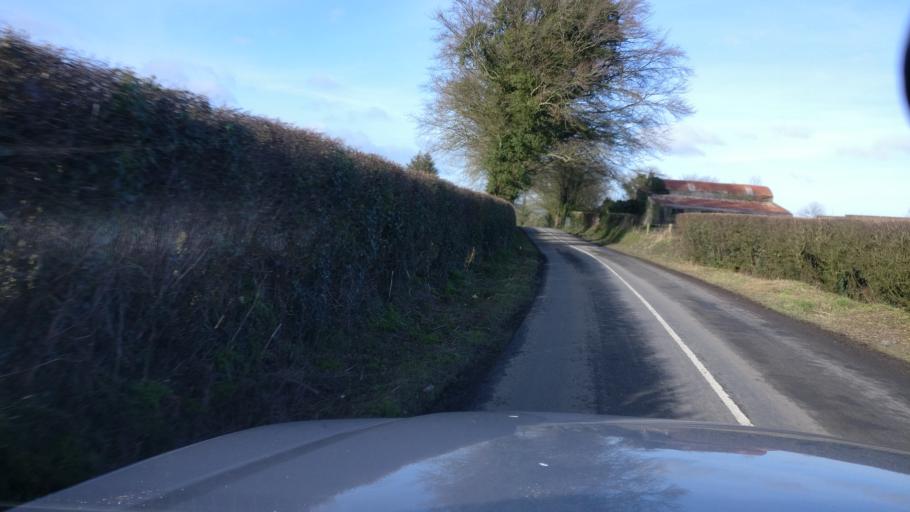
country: IE
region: Leinster
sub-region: Kilkenny
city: Castlecomer
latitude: 52.8778
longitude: -7.1626
